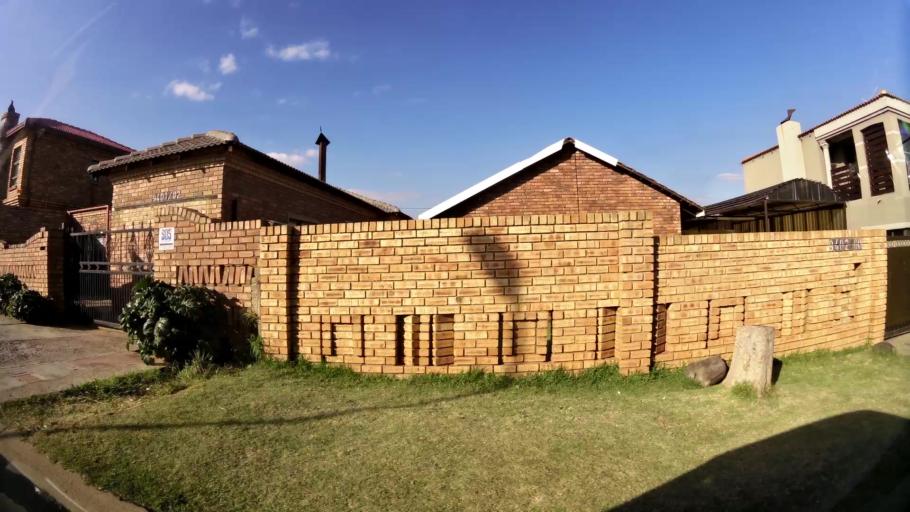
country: ZA
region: Gauteng
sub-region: City of Johannesburg Metropolitan Municipality
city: Soweto
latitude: -26.2731
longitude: 27.9155
